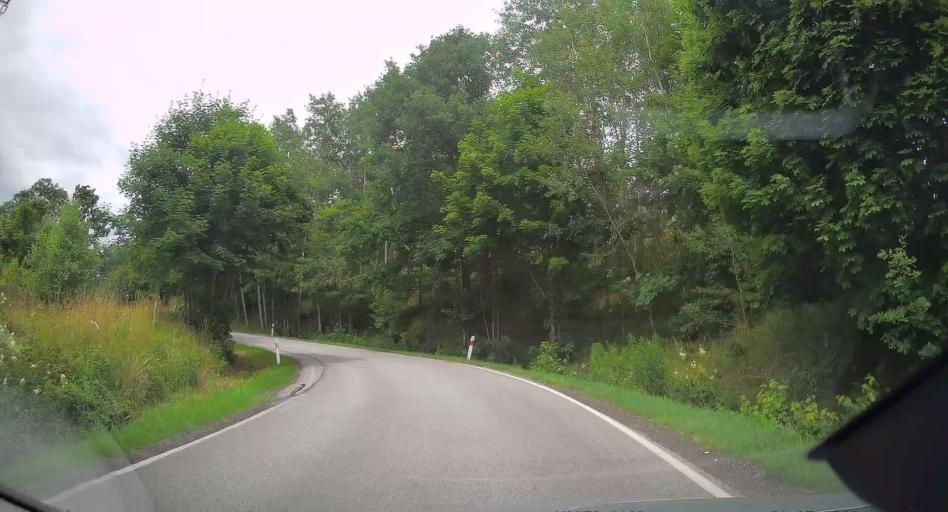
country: PL
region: Lower Silesian Voivodeship
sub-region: Powiat walbrzyski
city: Jedlina-Zdroj
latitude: 50.7338
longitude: 16.3571
